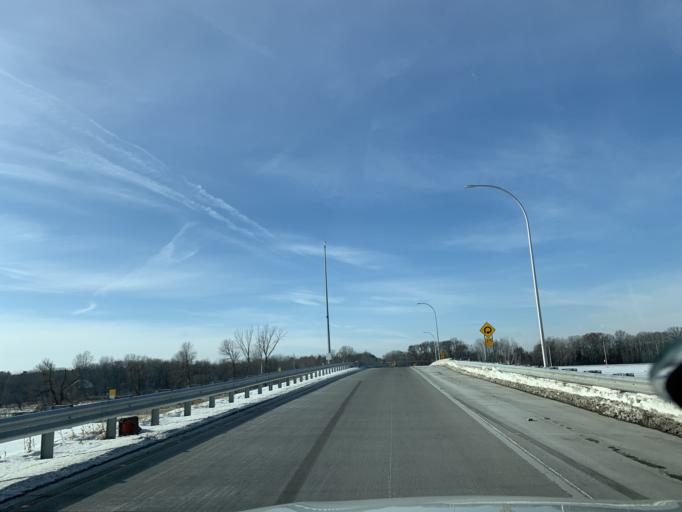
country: US
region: Minnesota
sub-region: Washington County
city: Forest Lake
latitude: 45.2899
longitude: -93.0015
